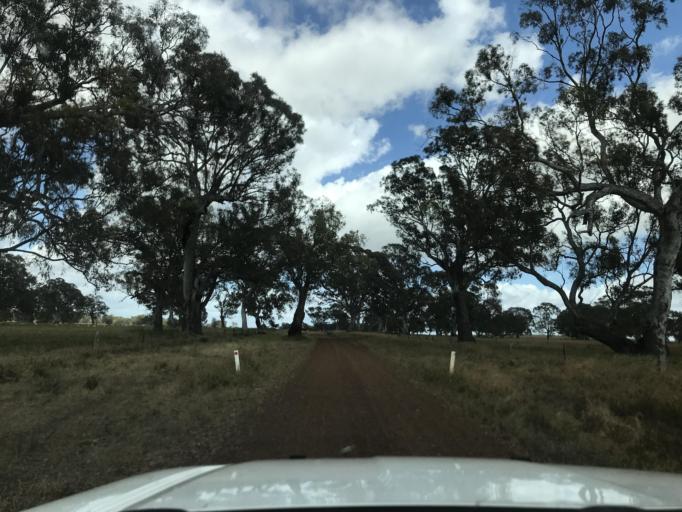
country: AU
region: South Australia
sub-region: Wattle Range
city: Penola
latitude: -37.1901
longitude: 141.4353
